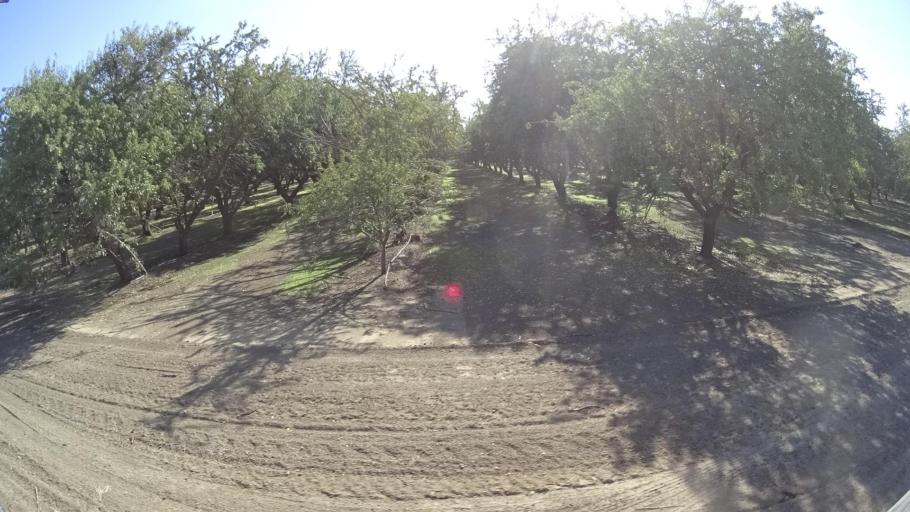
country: US
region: California
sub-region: Kern County
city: Wasco
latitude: 35.6668
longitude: -119.3410
